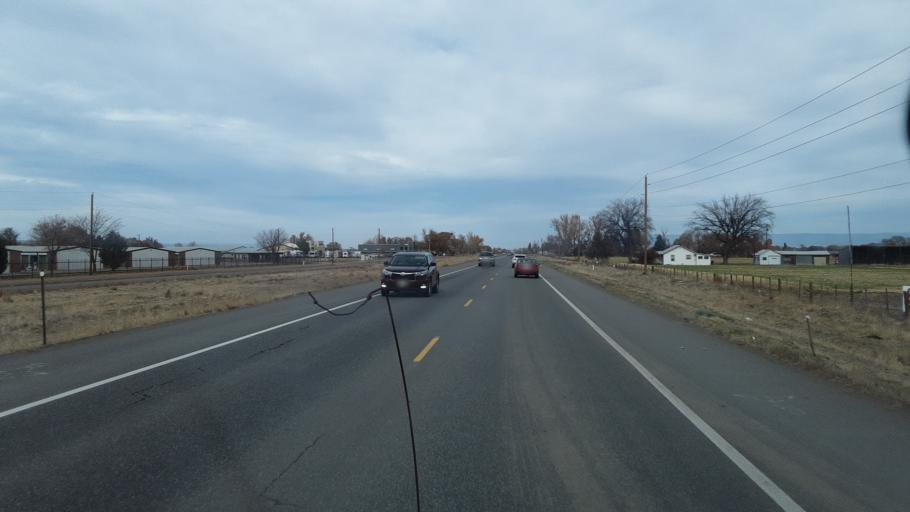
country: US
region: Colorado
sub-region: Montrose County
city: Montrose
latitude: 38.4022
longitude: -107.8397
